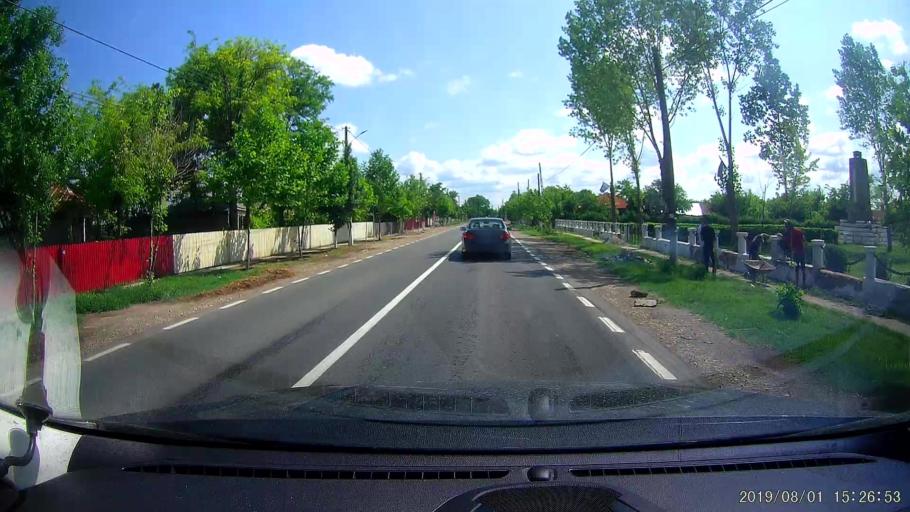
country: RO
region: Braila
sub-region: Comuna Viziru
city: Viziru
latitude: 45.0056
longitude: 27.7176
